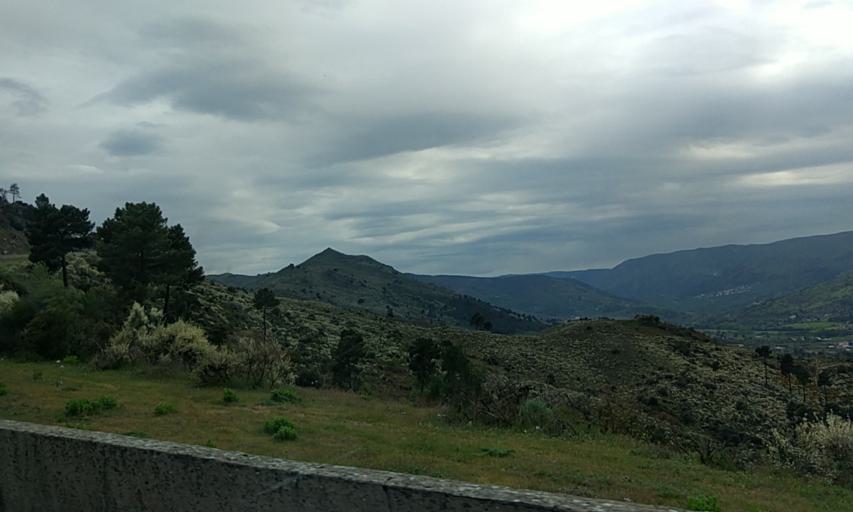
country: PT
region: Guarda
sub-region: Guarda
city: Guarda
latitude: 40.6015
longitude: -7.2753
